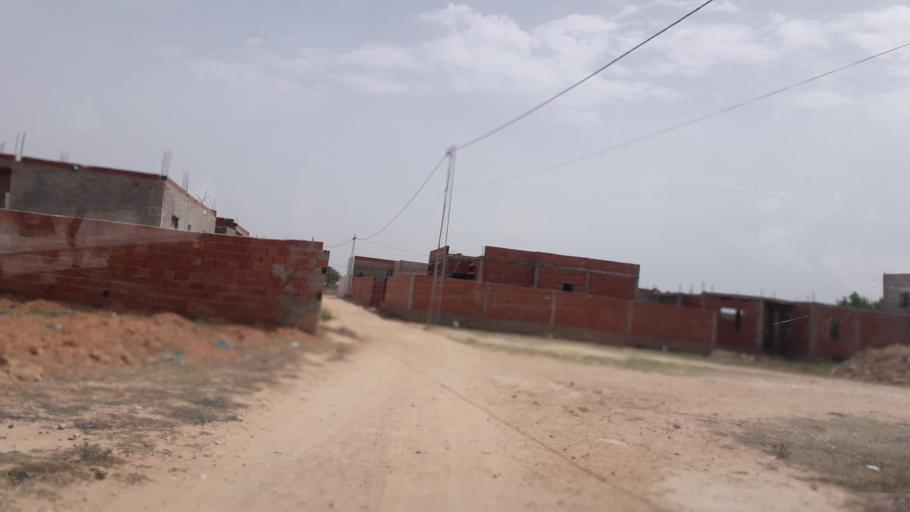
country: TN
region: Safaqis
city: Al Qarmadah
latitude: 34.8441
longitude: 10.7785
